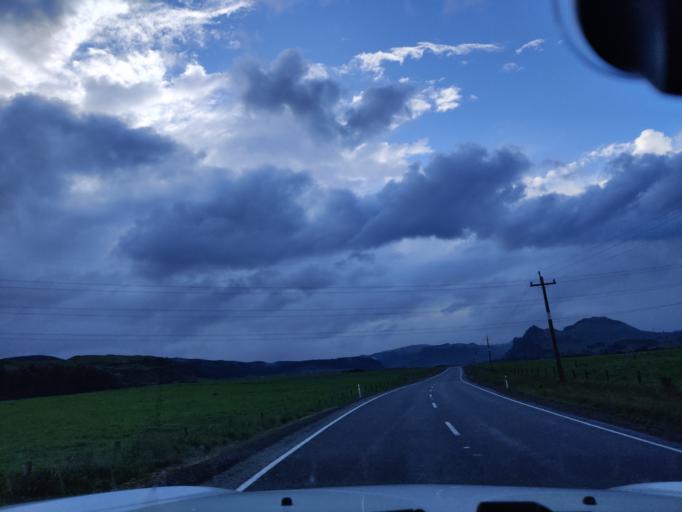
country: NZ
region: Waikato
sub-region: South Waikato District
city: Tokoroa
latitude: -38.3962
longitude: 175.7854
